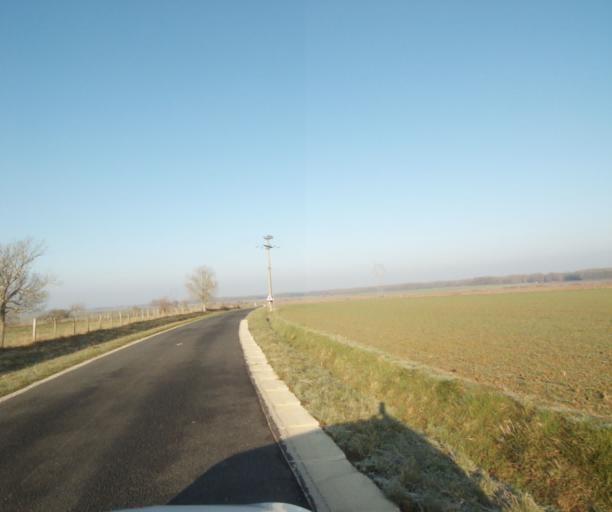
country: FR
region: Champagne-Ardenne
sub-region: Departement de la Haute-Marne
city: Montier-en-Der
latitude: 48.5043
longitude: 4.7355
